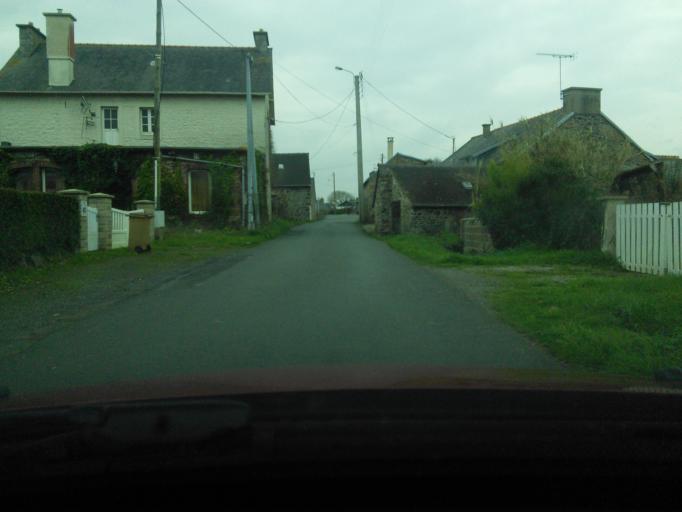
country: FR
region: Brittany
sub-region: Departement des Cotes-d'Armor
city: Hillion
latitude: 48.5298
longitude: -2.6664
